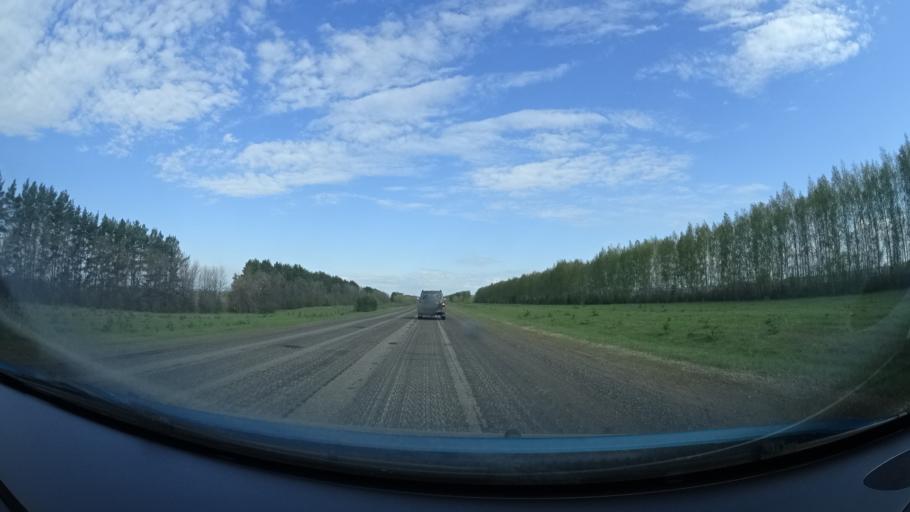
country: RU
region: Bashkortostan
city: Blagoveshchensk
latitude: 55.2231
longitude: 55.7945
